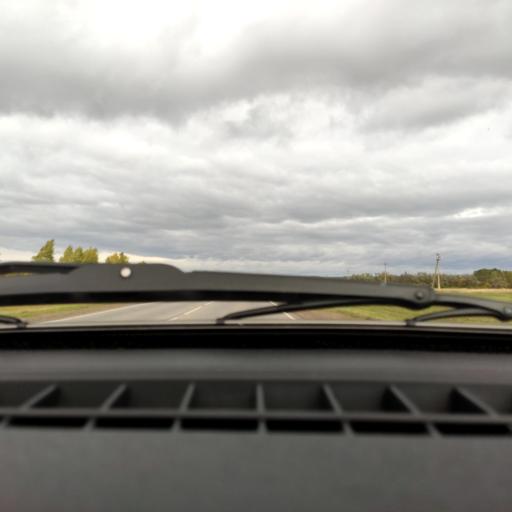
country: RU
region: Bashkortostan
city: Rayevskiy
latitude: 54.0214
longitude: 54.8854
